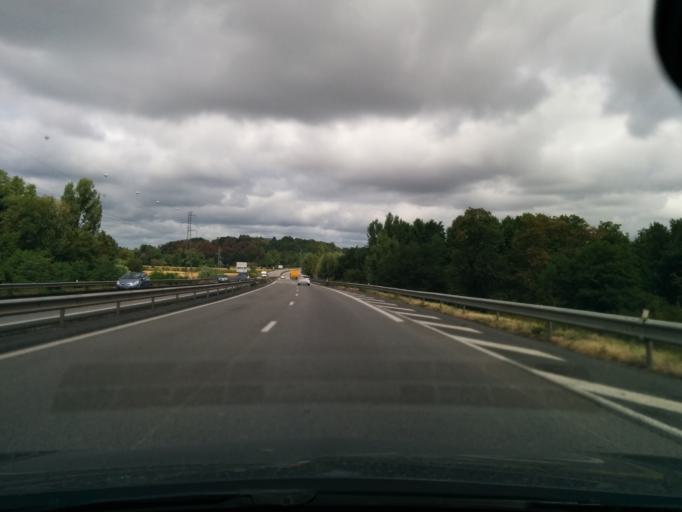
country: FR
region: Limousin
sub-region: Departement de la Correze
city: Saint-Pantaleon-de-Larche
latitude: 45.1572
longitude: 1.4825
